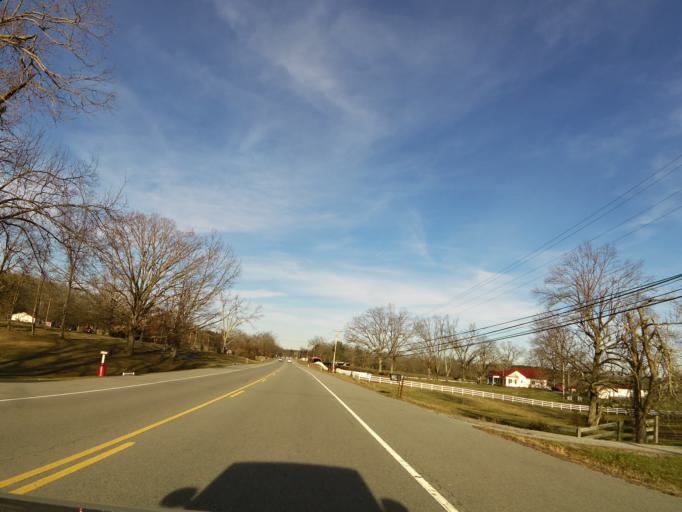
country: US
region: Tennessee
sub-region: White County
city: Sparta
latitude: 35.9423
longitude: -85.3265
